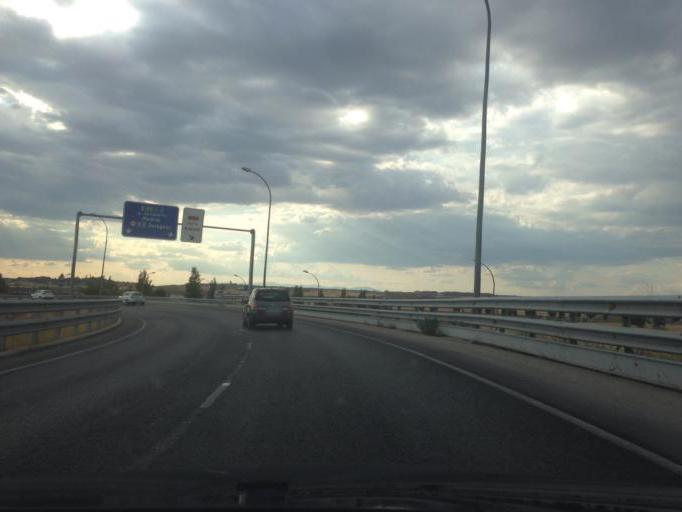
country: ES
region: Madrid
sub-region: Provincia de Madrid
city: Torrejon de Ardoz
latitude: 40.4658
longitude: -3.4821
